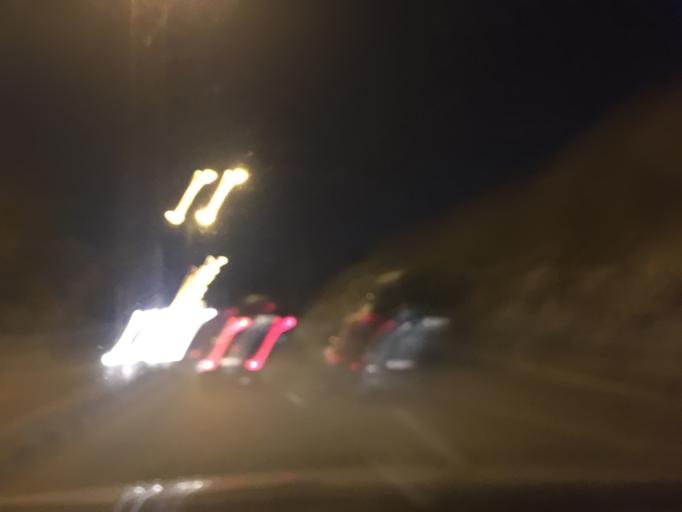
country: JO
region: Amman
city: Amman
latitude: 32.0002
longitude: 35.9321
